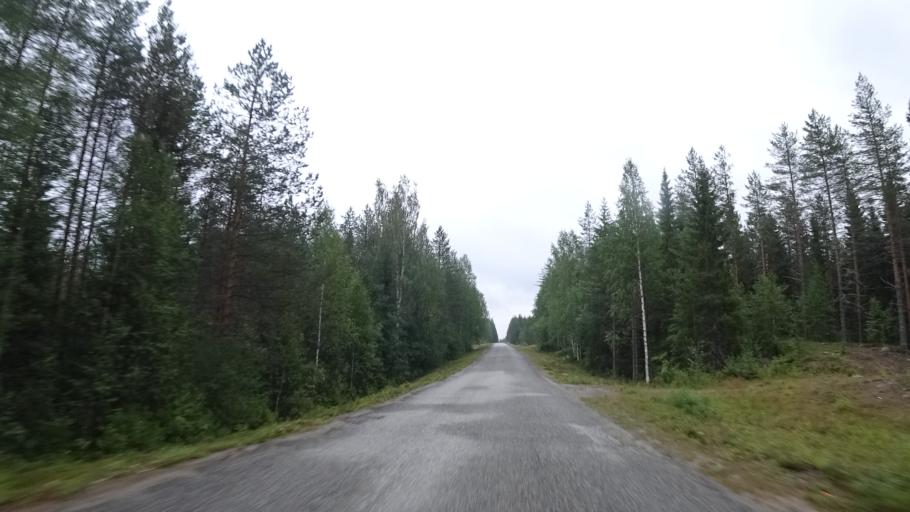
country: FI
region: North Karelia
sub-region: Joensuu
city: Ilomantsi
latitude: 63.2290
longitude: 30.8105
